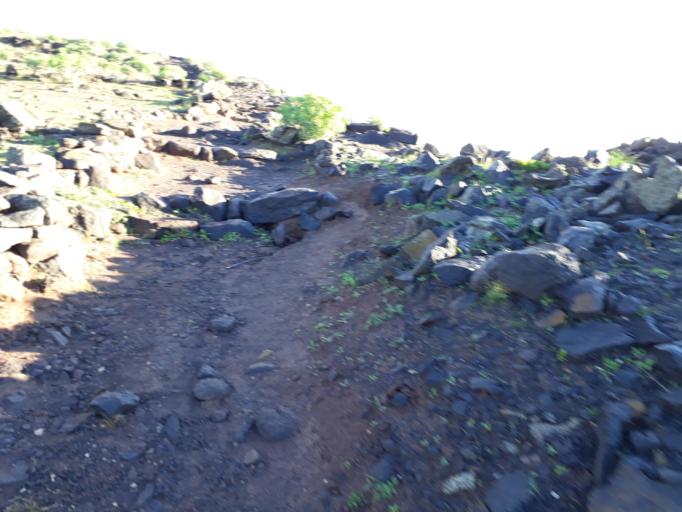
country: ES
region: Canary Islands
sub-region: Provincia de Santa Cruz de Tenerife
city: Vallehermosa
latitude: 28.1140
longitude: -17.3359
